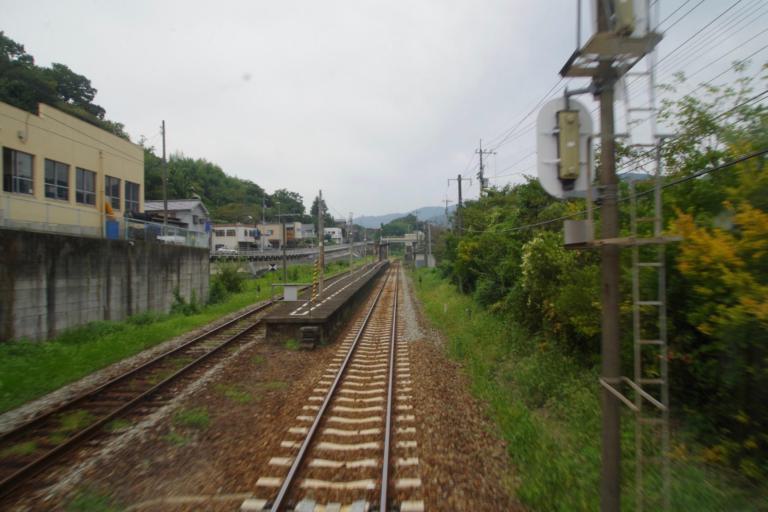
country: JP
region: Tokushima
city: Ikedacho
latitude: 34.0325
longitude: 133.8586
